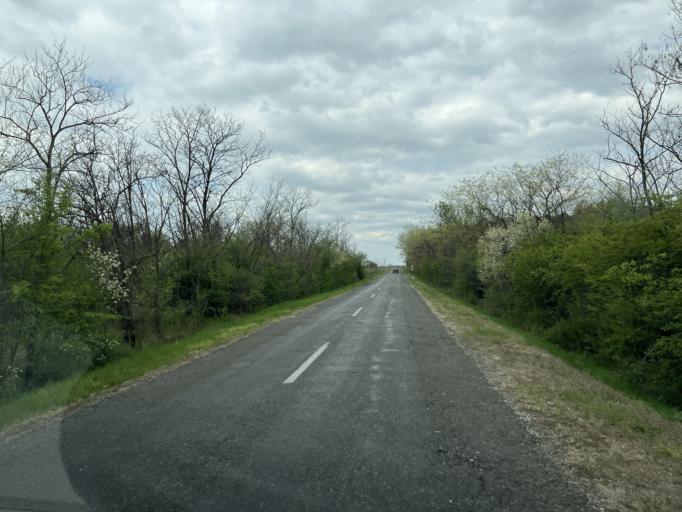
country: HU
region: Pest
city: Dabas
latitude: 47.1212
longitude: 19.3539
